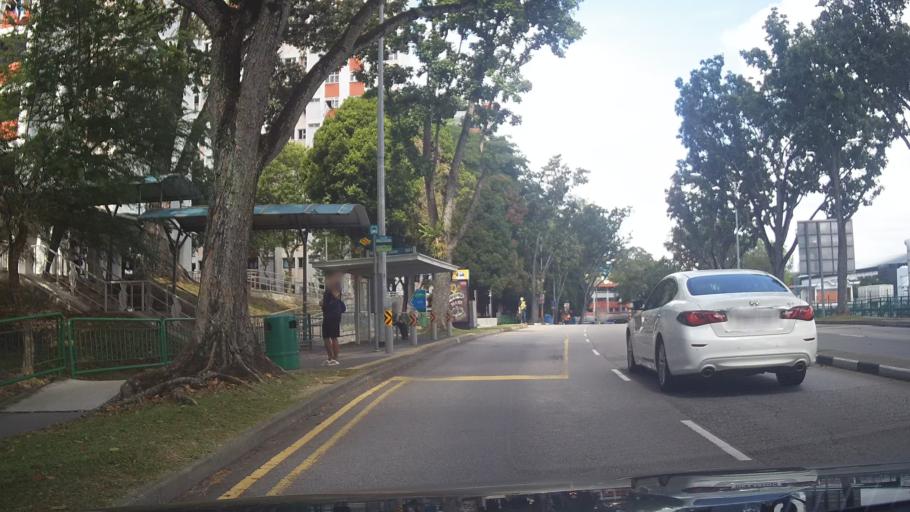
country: MY
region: Johor
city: Johor Bahru
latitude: 1.4420
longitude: 103.7788
